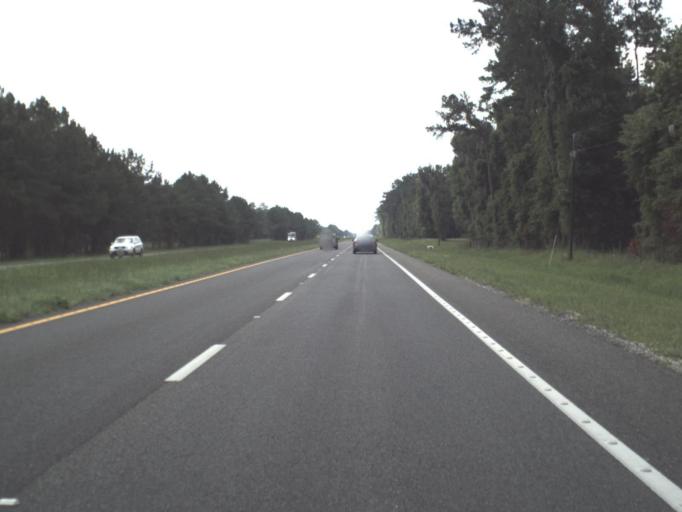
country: US
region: Florida
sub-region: Levy County
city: Chiefland
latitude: 29.4436
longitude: -82.8398
